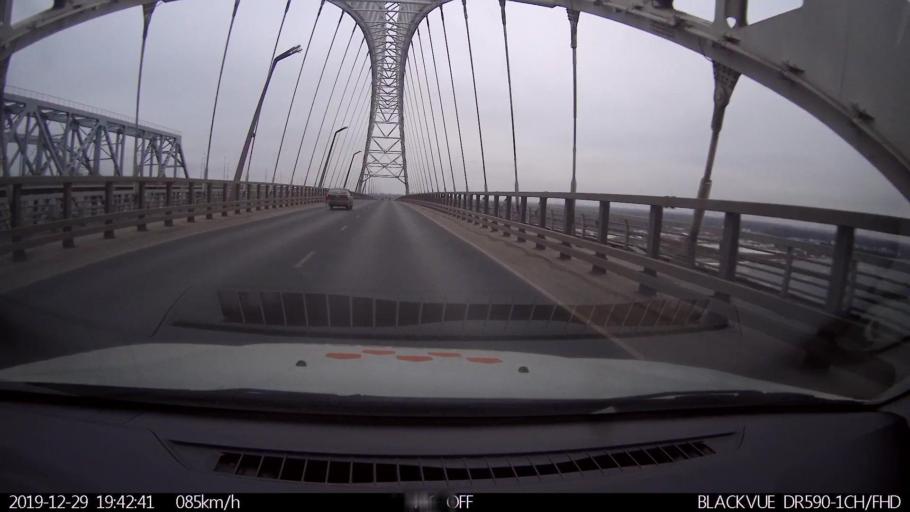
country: RU
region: Nizjnij Novgorod
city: Neklyudovo
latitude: 56.3526
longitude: 43.9242
